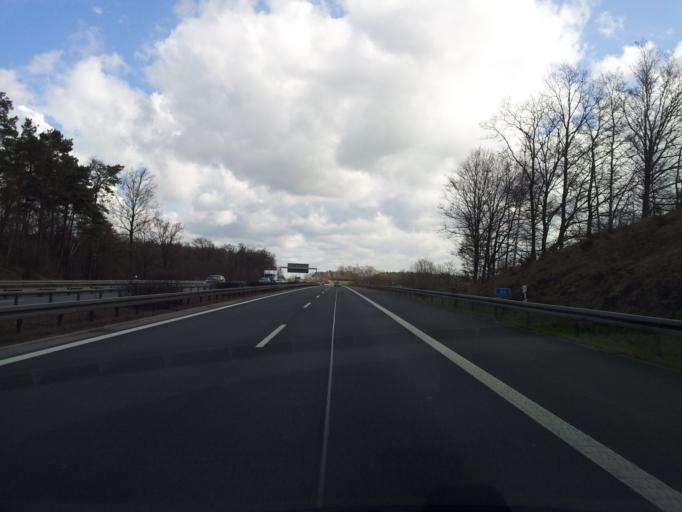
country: DE
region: Saxony
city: Albertstadt
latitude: 51.1471
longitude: 13.7698
